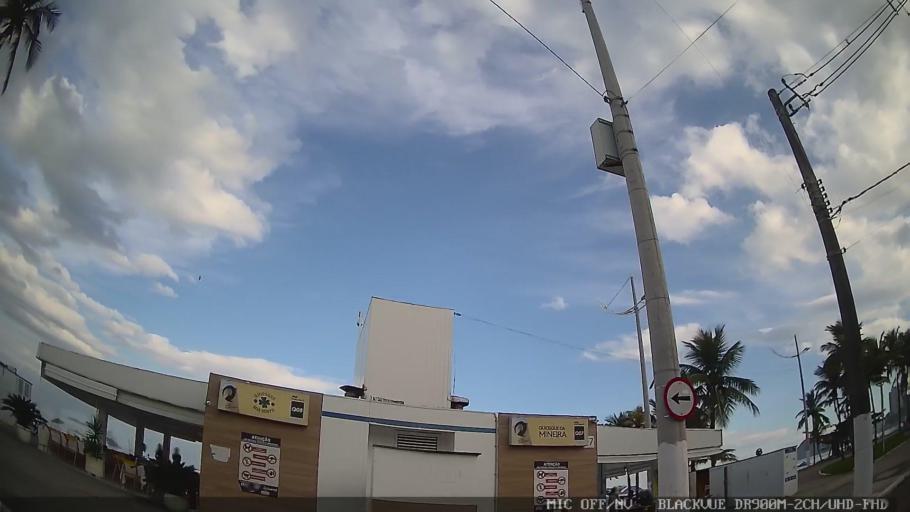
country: BR
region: Sao Paulo
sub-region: Guaruja
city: Guaruja
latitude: -23.9891
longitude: -46.2393
